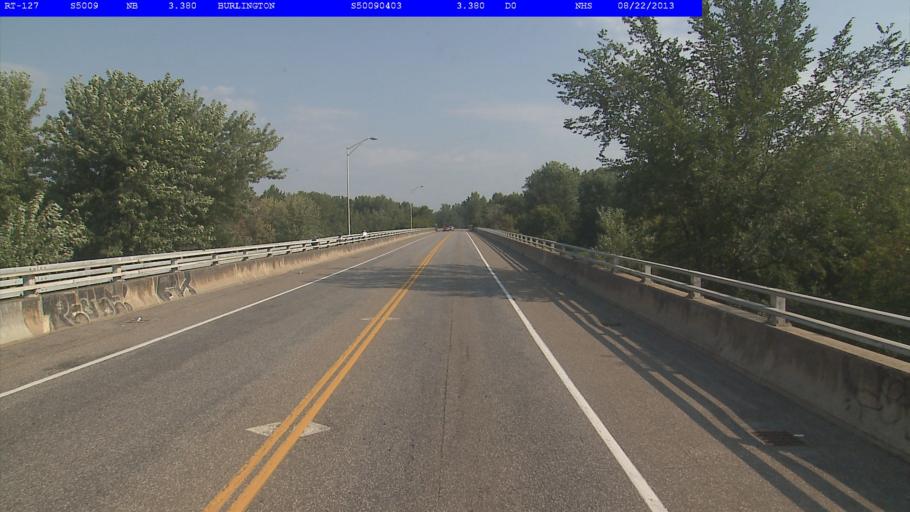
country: US
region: Vermont
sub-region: Chittenden County
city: Burlington
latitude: 44.5241
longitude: -73.2554
